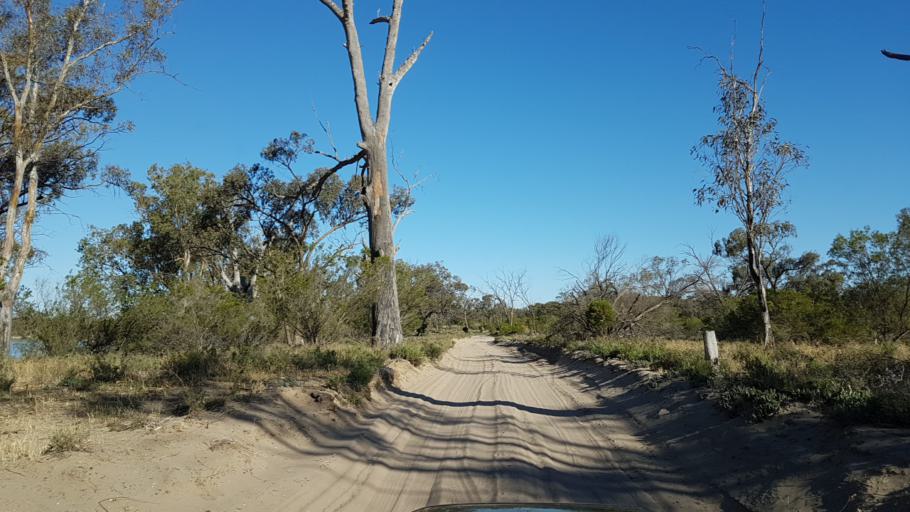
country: AU
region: South Australia
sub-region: Loxton Waikerie
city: Waikerie
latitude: -34.1586
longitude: 140.0277
